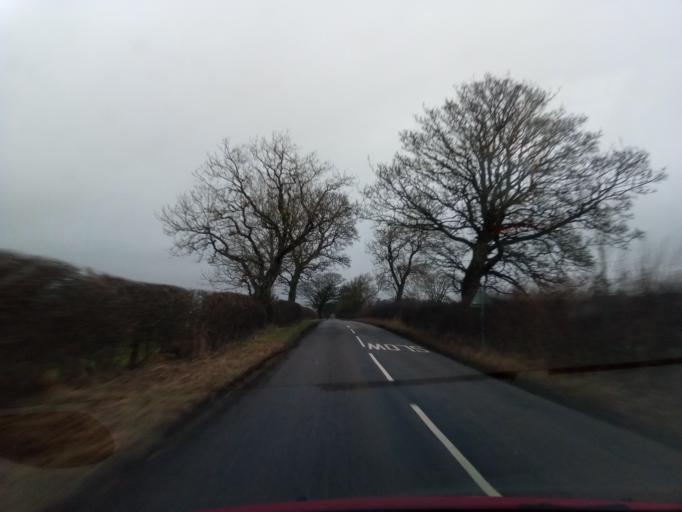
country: GB
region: England
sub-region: Northumberland
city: Rothley
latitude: 55.1876
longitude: -1.9700
